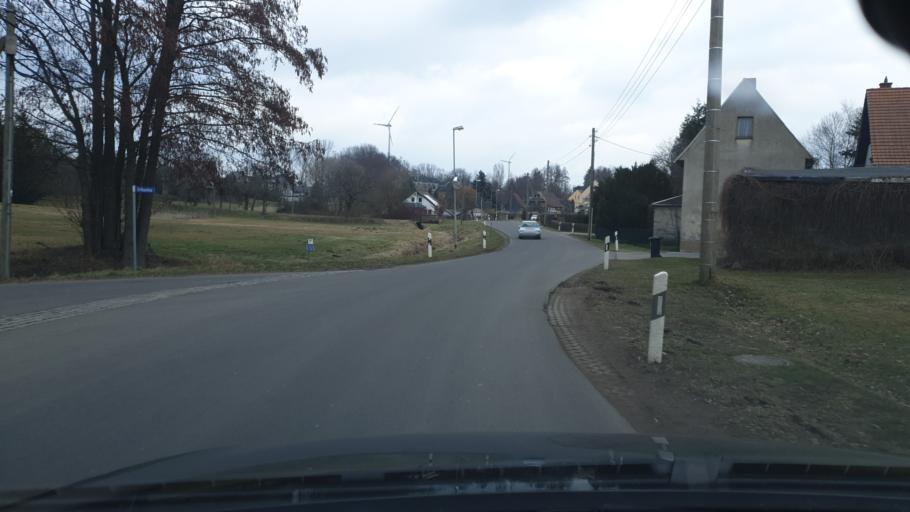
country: DE
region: Saxony
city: Erlau
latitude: 51.0051
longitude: 12.9213
